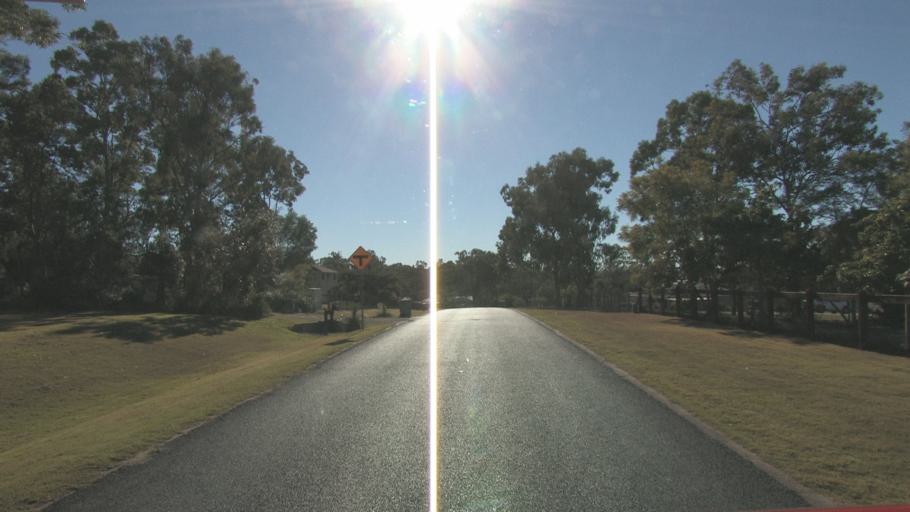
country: AU
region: Queensland
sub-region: Logan
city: North Maclean
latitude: -27.7434
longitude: 152.9631
